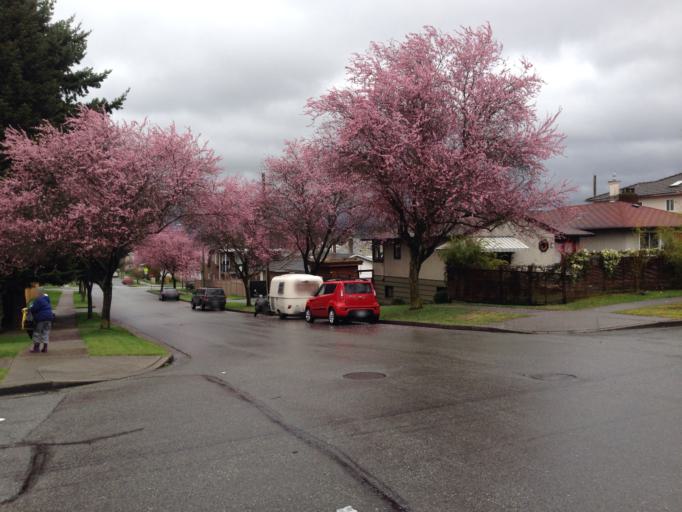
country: CA
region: British Columbia
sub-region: Fraser Valley Regional District
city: North Vancouver
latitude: 49.2704
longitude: -123.0365
